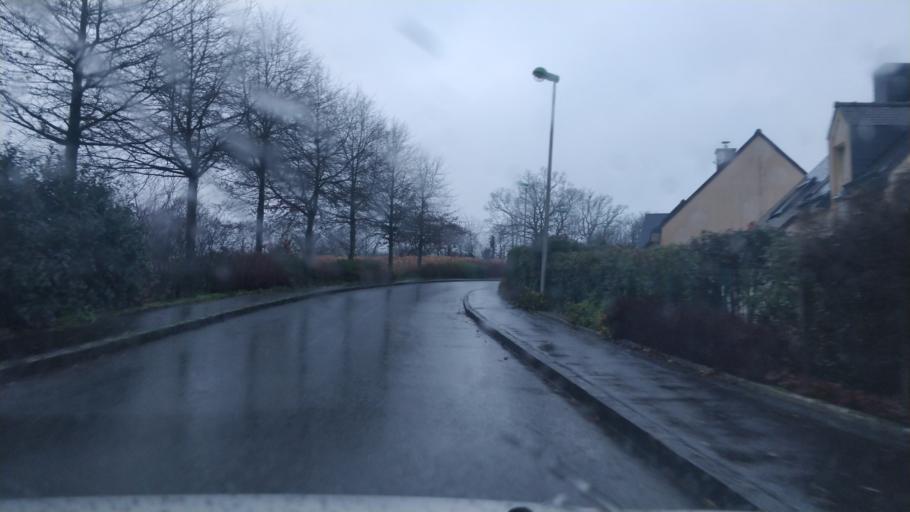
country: FR
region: Brittany
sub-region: Departement d'Ille-et-Vilaine
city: Liffre
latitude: 48.2130
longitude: -1.4984
